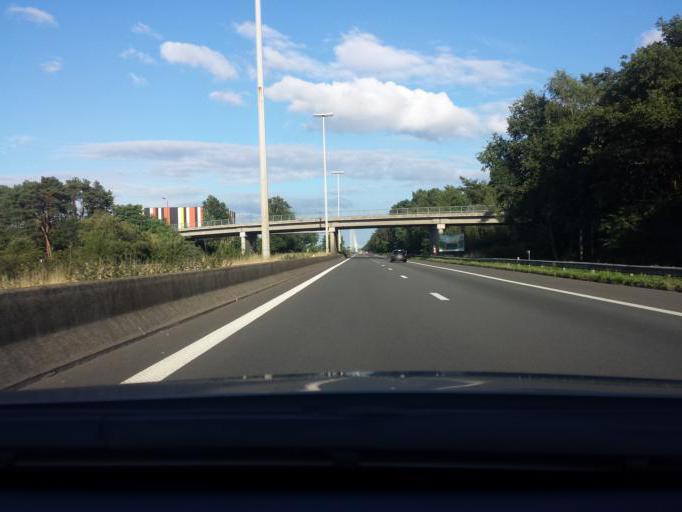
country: BE
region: Flanders
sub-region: Provincie Antwerpen
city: Olen
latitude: 51.1479
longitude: 4.8714
